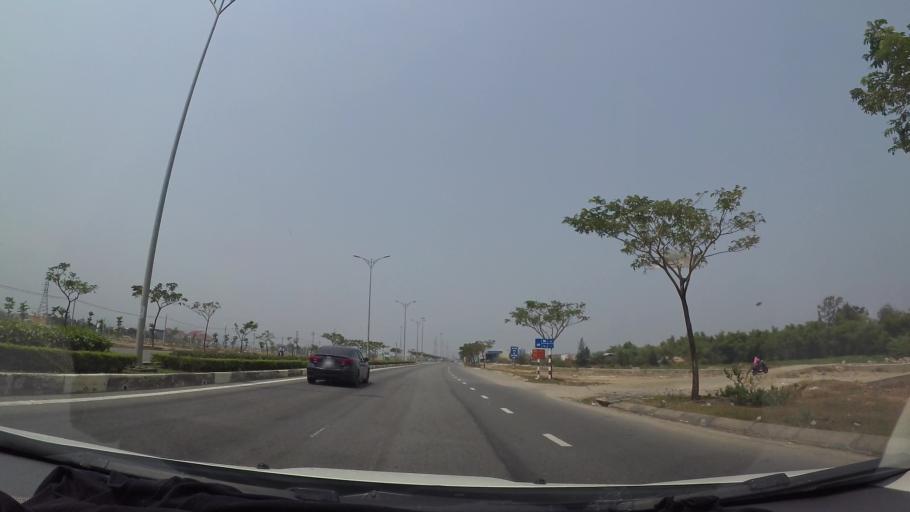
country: VN
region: Da Nang
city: Ngu Hanh Son
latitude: 15.9924
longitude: 108.2367
